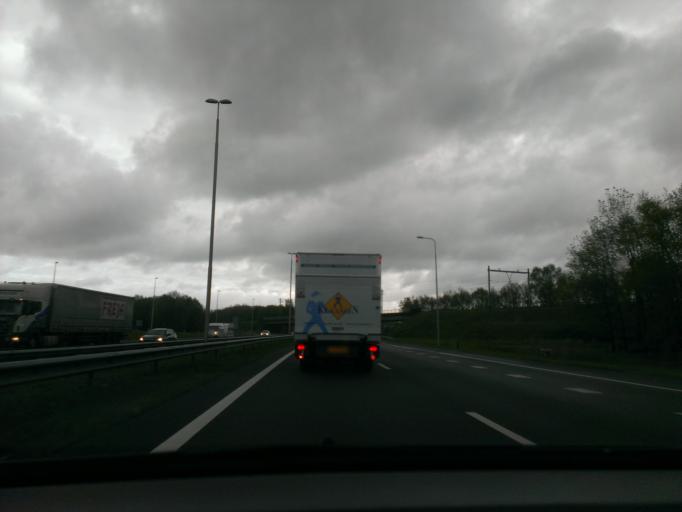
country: NL
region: Overijssel
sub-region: Gemeente Staphorst
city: Staphorst
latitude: 52.6674
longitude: 6.1986
